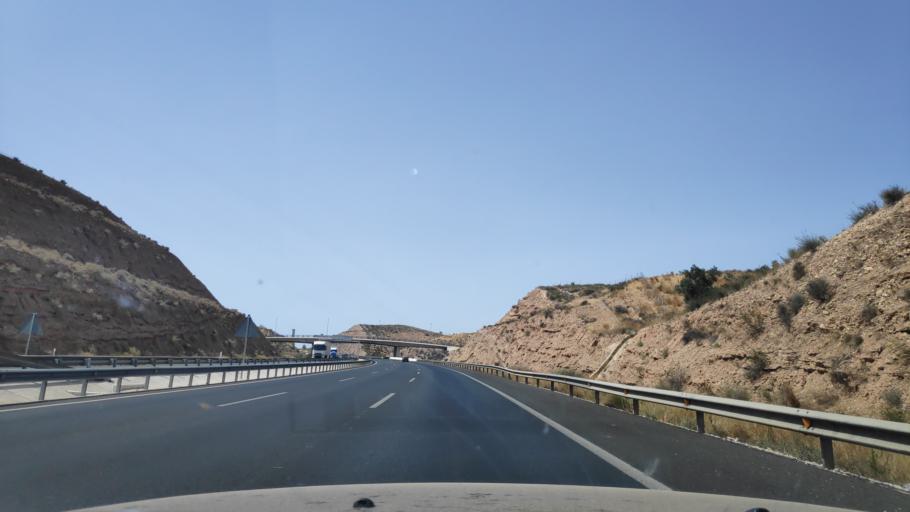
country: ES
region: Murcia
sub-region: Murcia
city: Molina de Segura
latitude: 38.0385
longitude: -1.1608
